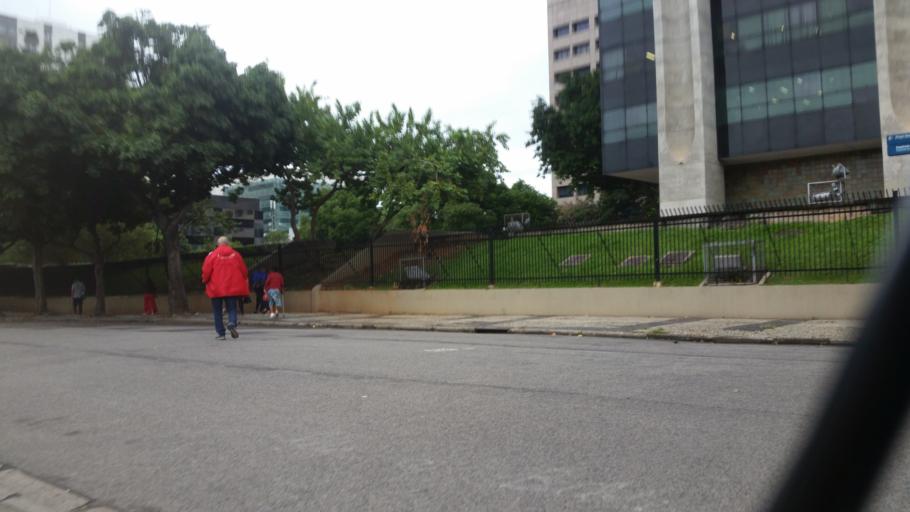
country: BR
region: Rio de Janeiro
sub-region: Rio De Janeiro
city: Rio de Janeiro
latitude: -22.9108
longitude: -43.2055
